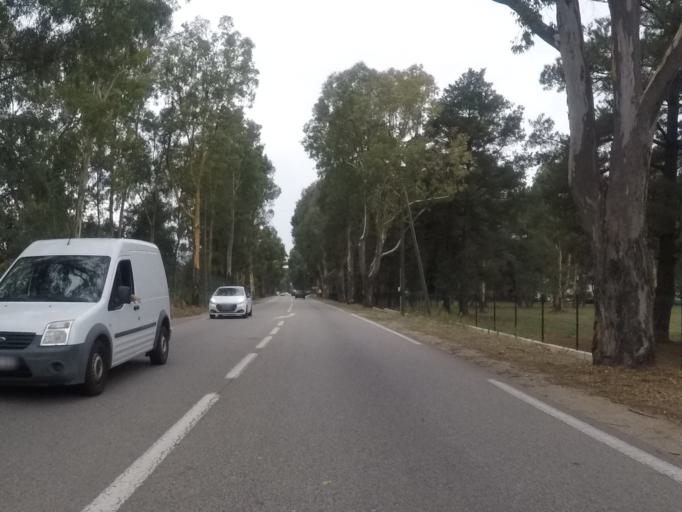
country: FR
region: Corsica
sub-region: Departement de la Corse-du-Sud
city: Afa
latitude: 41.9775
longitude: 8.8292
